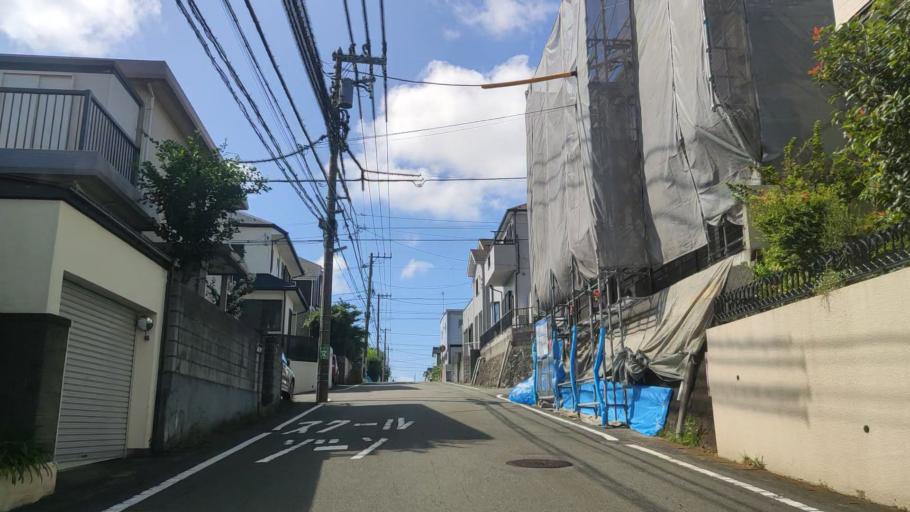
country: JP
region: Kanagawa
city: Yokohama
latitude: 35.4087
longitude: 139.5726
